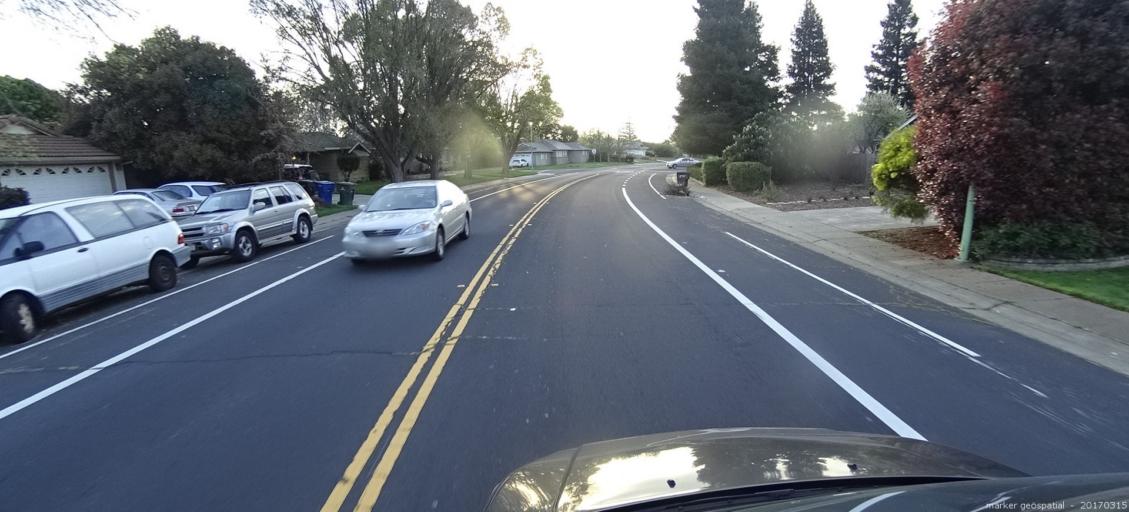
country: US
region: California
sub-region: Sacramento County
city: Parkway
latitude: 38.5073
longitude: -121.5125
